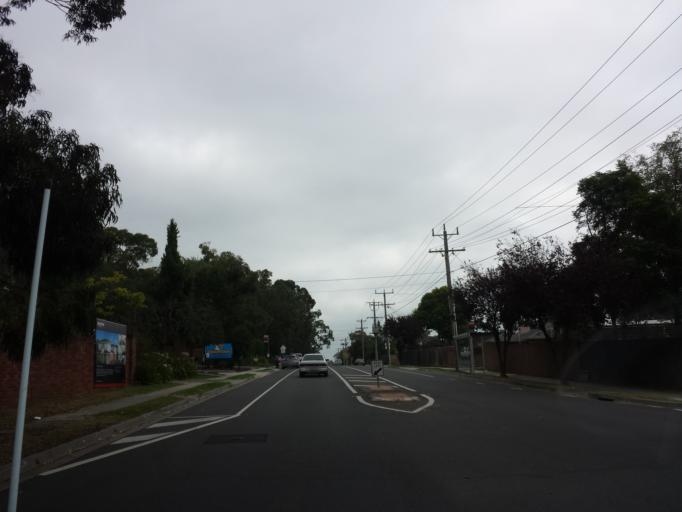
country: AU
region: Victoria
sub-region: Knox
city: The Basin
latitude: -37.8467
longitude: 145.2996
